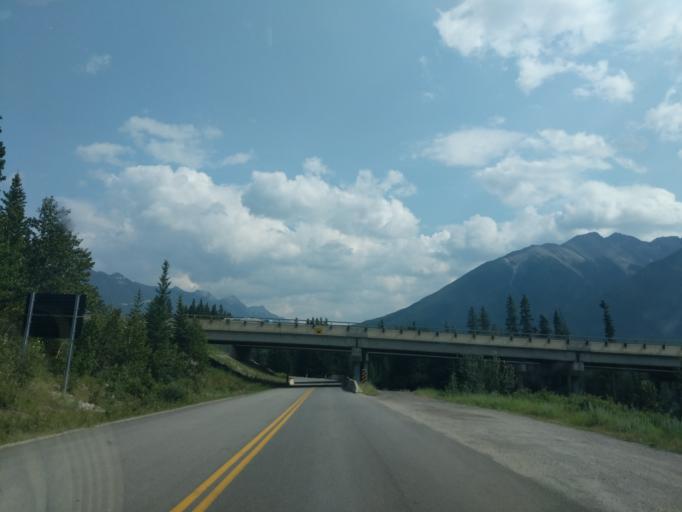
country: CA
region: Alberta
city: Banff
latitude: 51.1697
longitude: -115.6586
